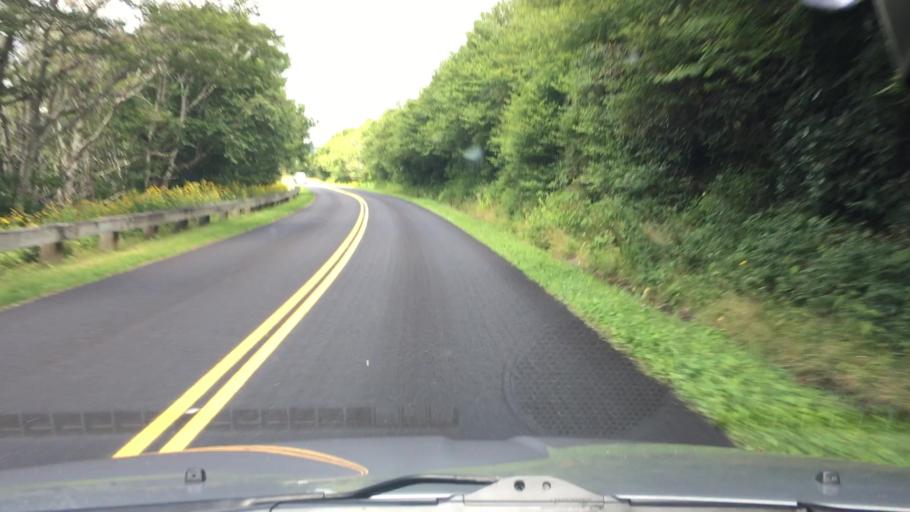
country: US
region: North Carolina
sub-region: Buncombe County
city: Black Mountain
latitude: 35.7204
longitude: -82.3555
